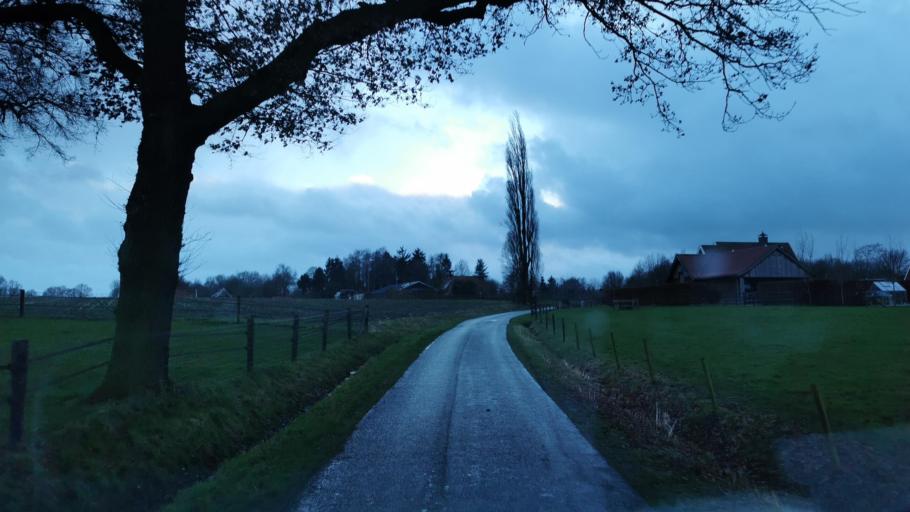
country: NL
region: Overijssel
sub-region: Gemeente Oldenzaal
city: Oldenzaal
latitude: 52.3254
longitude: 6.9371
